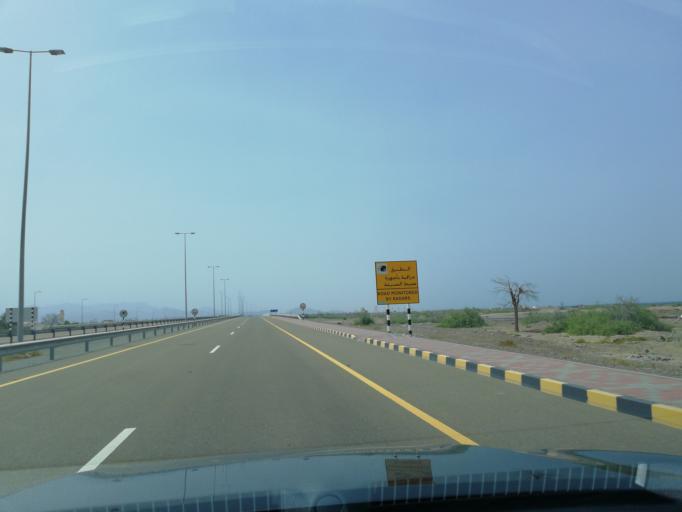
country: OM
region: Al Batinah
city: Shinas
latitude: 24.8670
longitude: 56.4107
